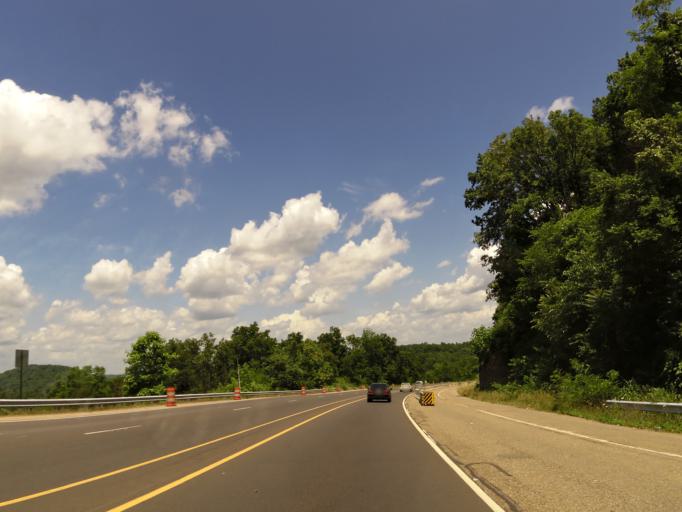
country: US
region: Tennessee
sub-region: Union County
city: Condon
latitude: 36.1403
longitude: -83.9153
